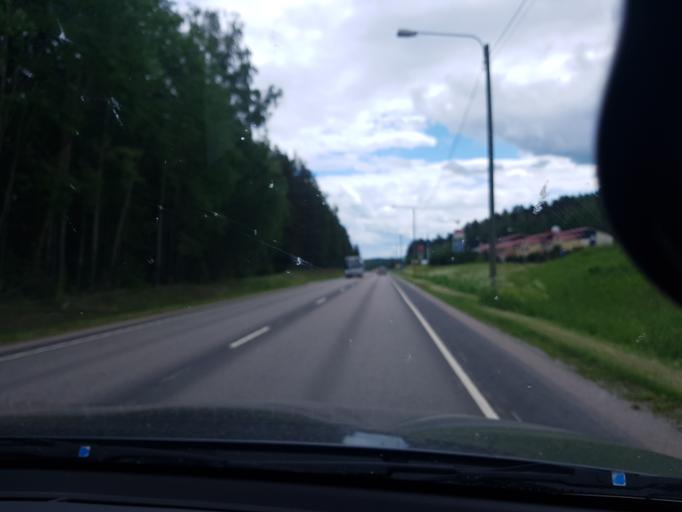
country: FI
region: Pirkanmaa
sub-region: Tampere
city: Paelkaene
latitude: 61.3494
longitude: 24.2553
